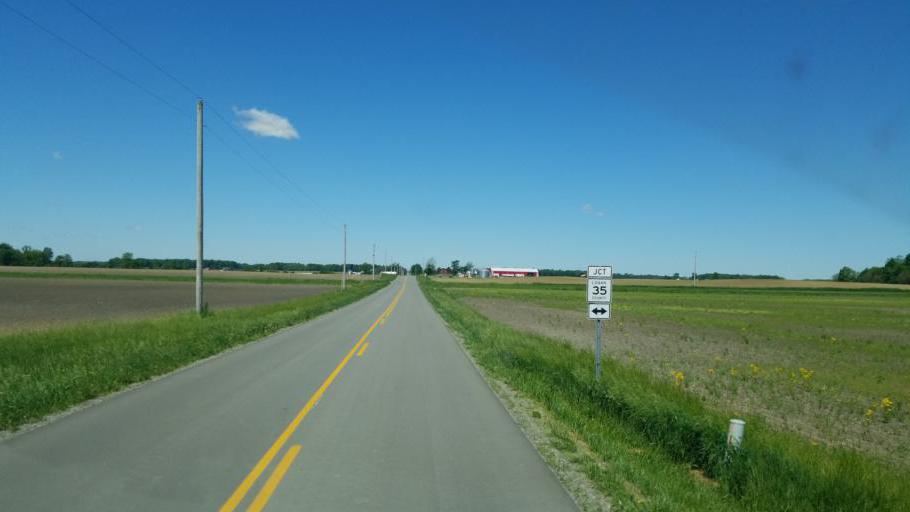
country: US
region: Ohio
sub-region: Shelby County
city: Jackson Center
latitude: 40.4174
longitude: -83.9724
